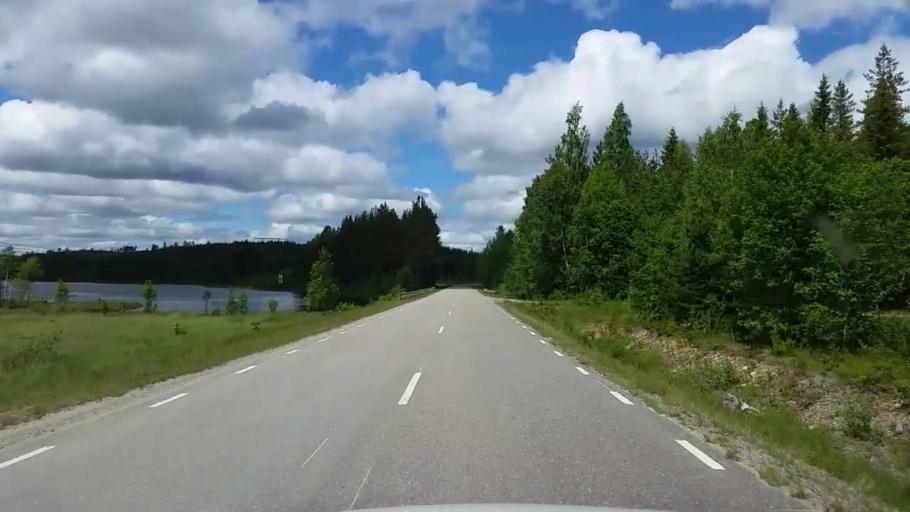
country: SE
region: Gaevleborg
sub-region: Bollnas Kommun
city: Vittsjo
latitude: 61.1499
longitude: 16.1610
